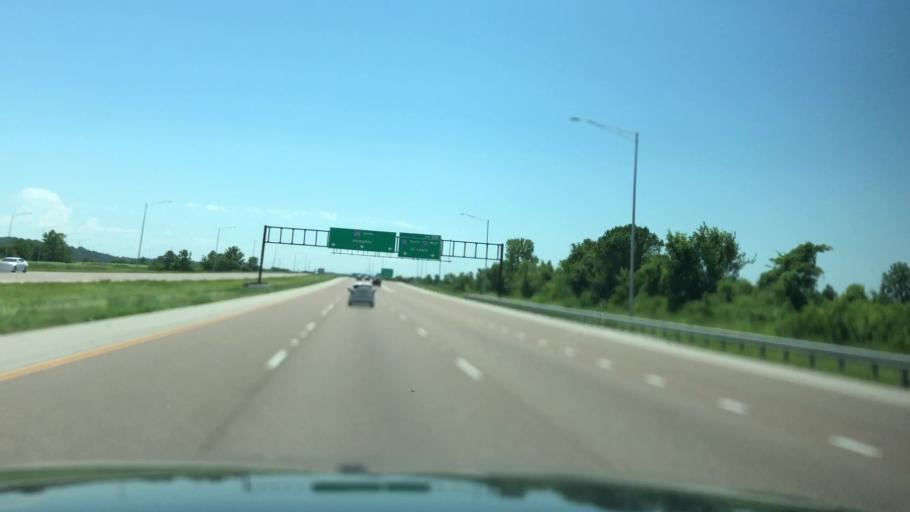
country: US
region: Illinois
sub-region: Saint Clair County
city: Caseyville
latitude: 38.6823
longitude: -90.0303
